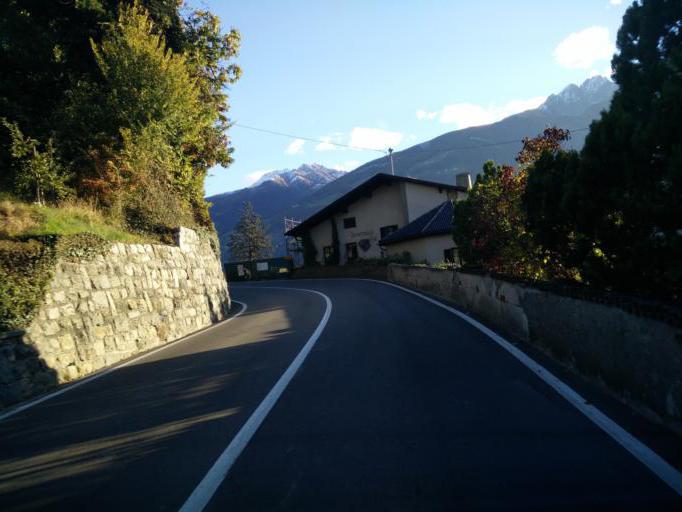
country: IT
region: Trentino-Alto Adige
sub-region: Bolzano
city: Caines
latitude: 46.6914
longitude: 11.1707
